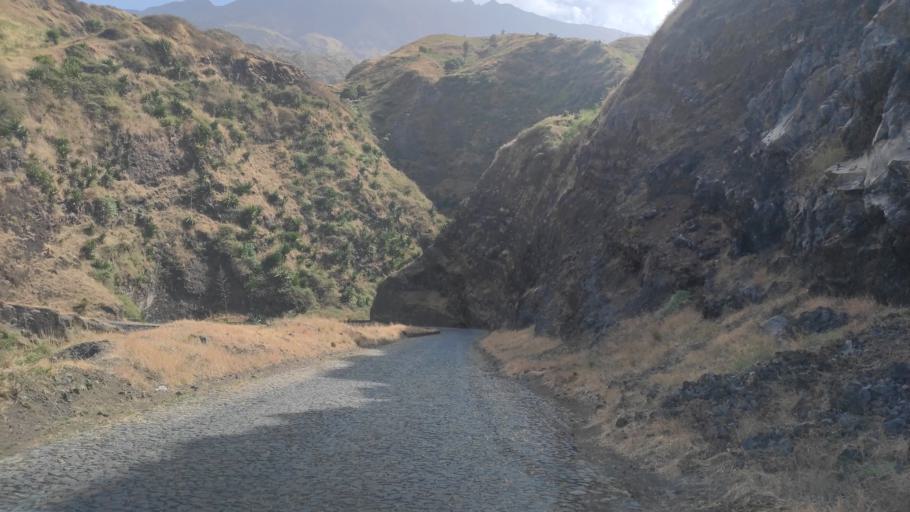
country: CV
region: Mosteiros
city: Porto dos Mosteiros
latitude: 15.0200
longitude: -24.3958
